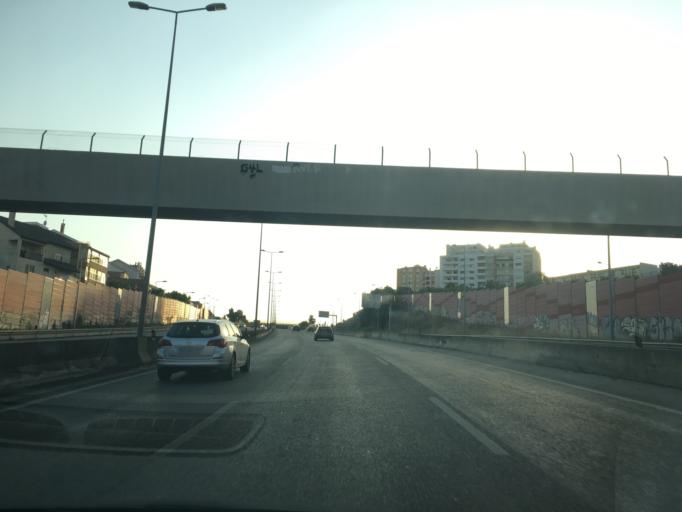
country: PT
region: Lisbon
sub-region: Sintra
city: Cacem
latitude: 38.7660
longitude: -9.3014
